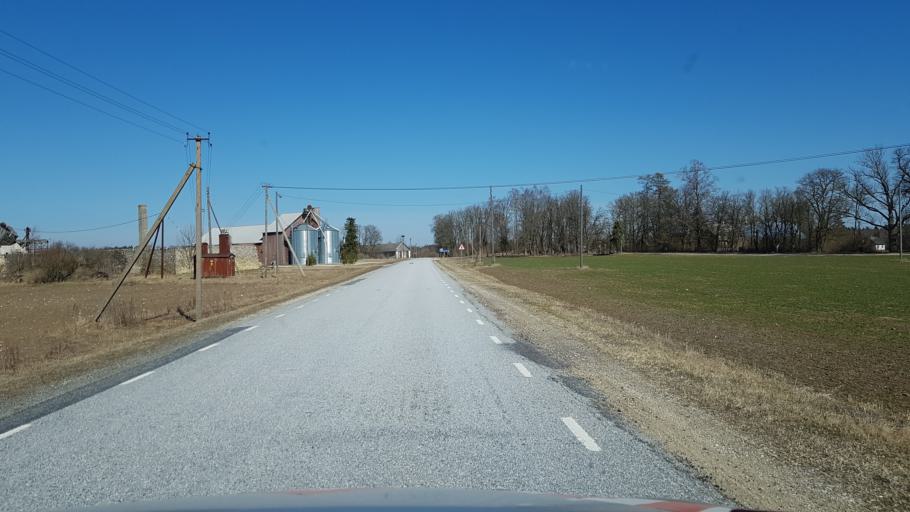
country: EE
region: Laeaene-Virumaa
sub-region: Tamsalu vald
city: Tamsalu
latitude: 59.0660
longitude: 26.1106
